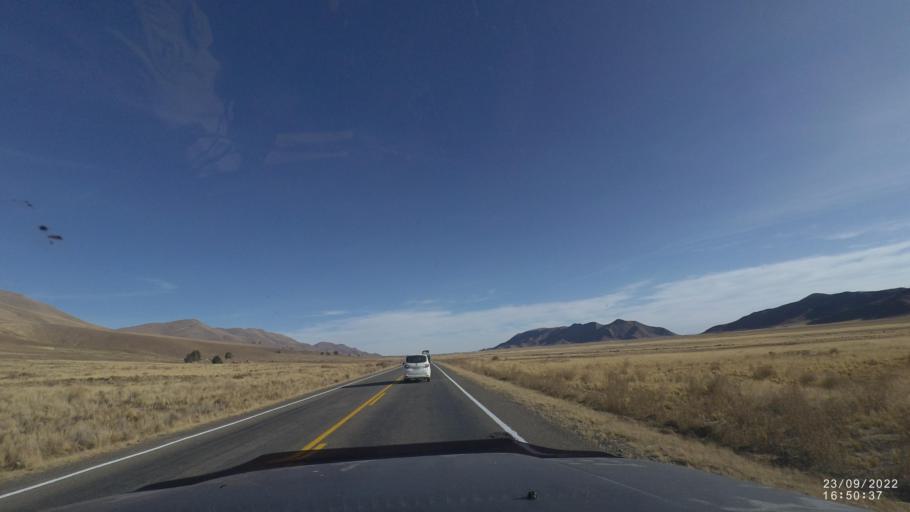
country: BO
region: Oruro
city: Poopo
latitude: -18.4045
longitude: -66.9771
